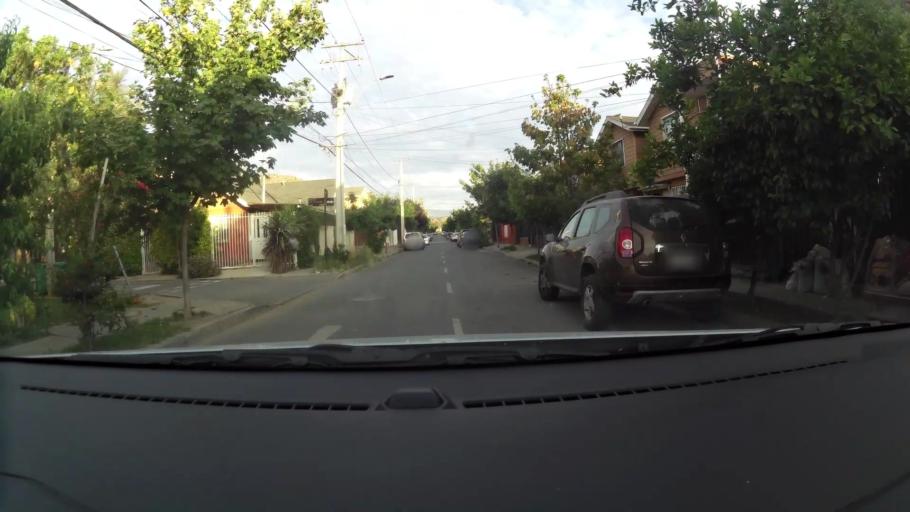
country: CL
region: Santiago Metropolitan
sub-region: Provincia de Maipo
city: San Bernardo
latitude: -33.6245
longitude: -70.6914
